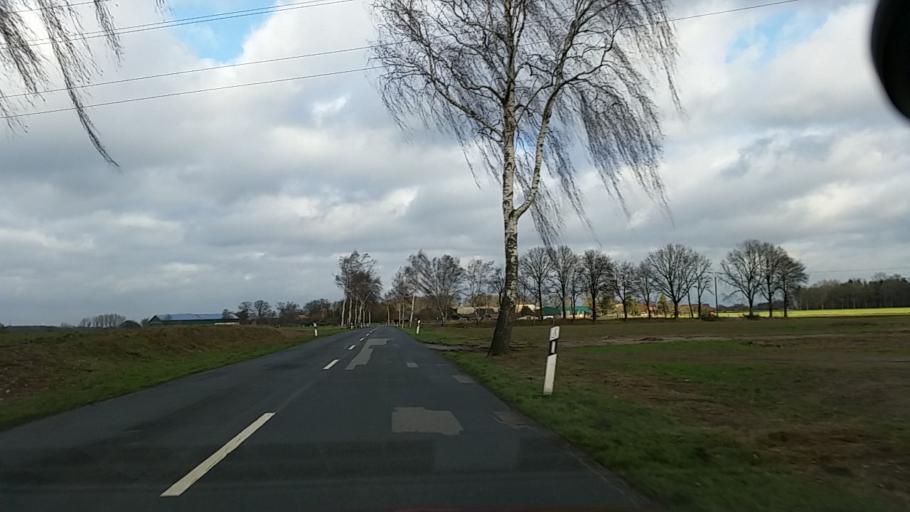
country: DE
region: Lower Saxony
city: Wittingen
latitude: 52.7016
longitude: 10.7474
